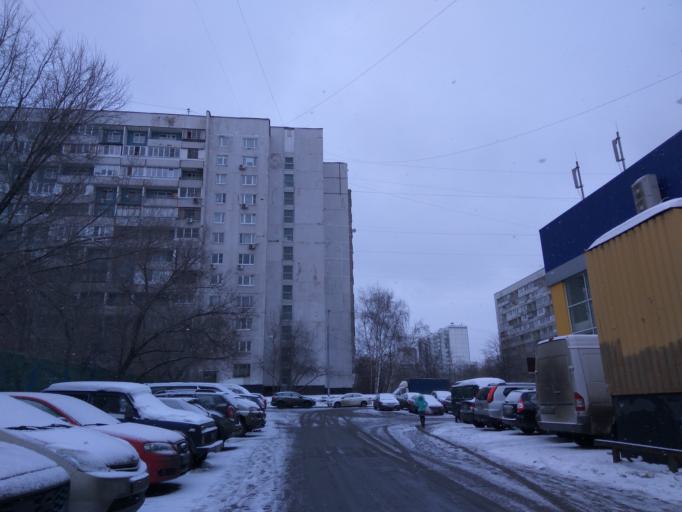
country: RU
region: Moscow
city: Strogino
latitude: 55.7972
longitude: 37.4019
